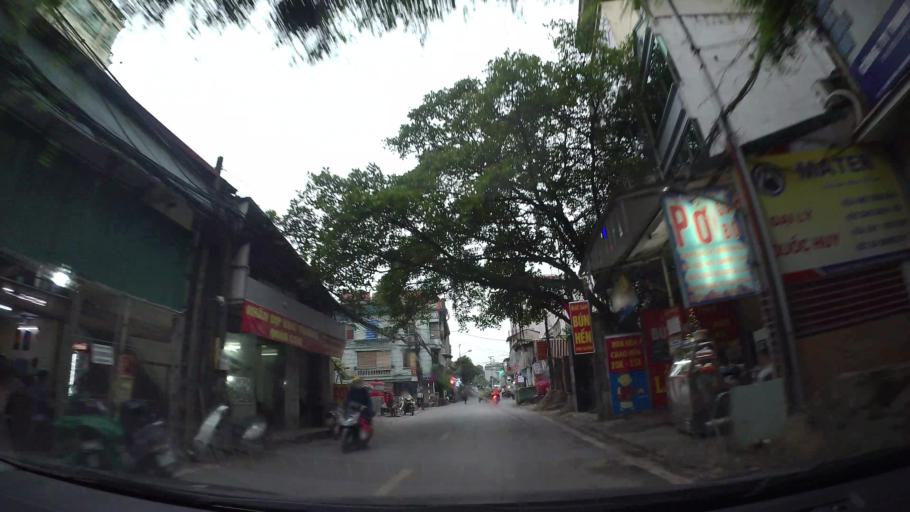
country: VN
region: Ha Noi
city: Hai BaTrung
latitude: 21.0093
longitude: 105.8667
